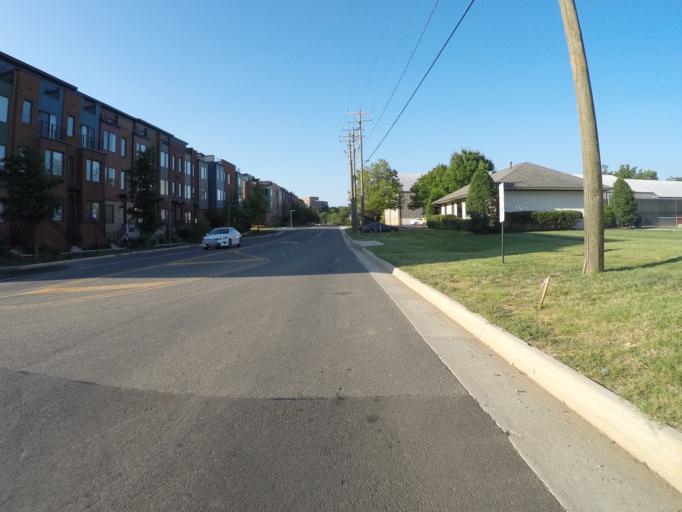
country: US
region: Virginia
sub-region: Fairfax County
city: Merrifield
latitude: 38.8709
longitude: -77.2327
